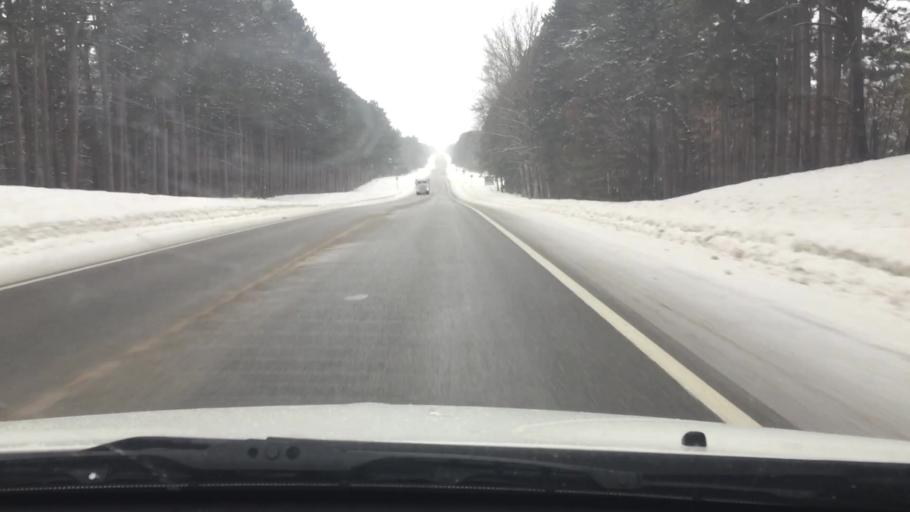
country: US
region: Michigan
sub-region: Otsego County
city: Gaylord
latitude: 45.0618
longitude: -84.8108
